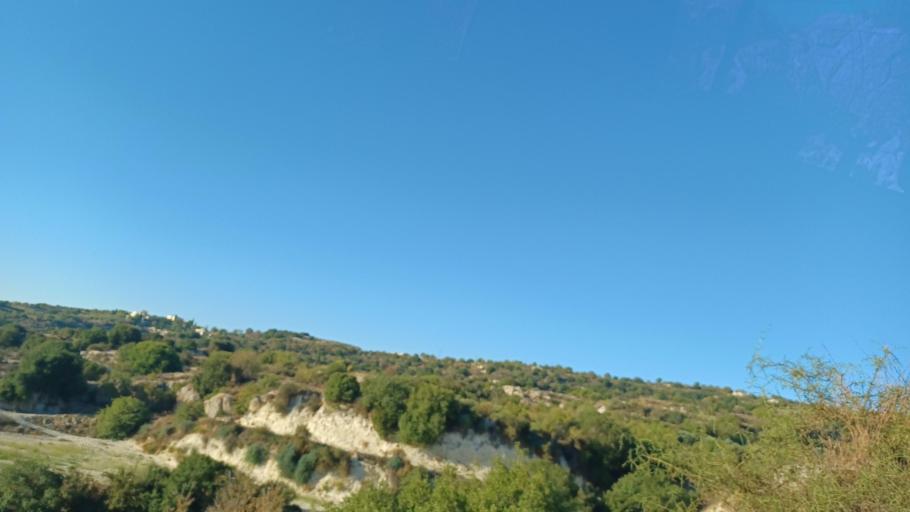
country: CY
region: Pafos
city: Mesogi
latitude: 34.8610
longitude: 32.5272
